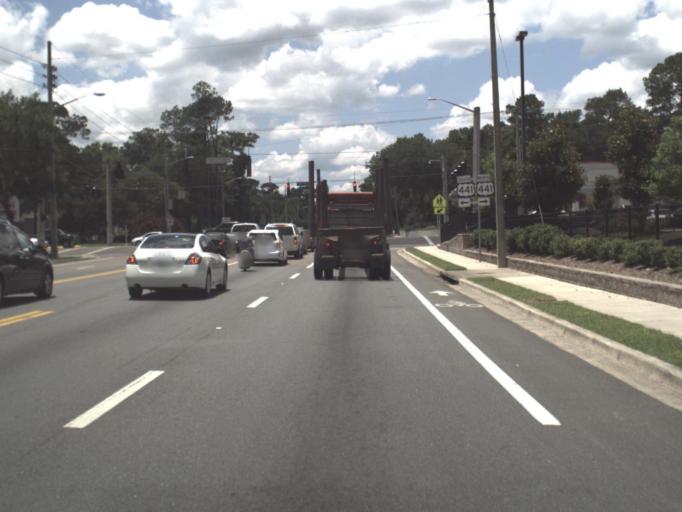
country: US
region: Florida
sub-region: Alachua County
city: Gainesville
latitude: 29.6886
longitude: -82.3381
